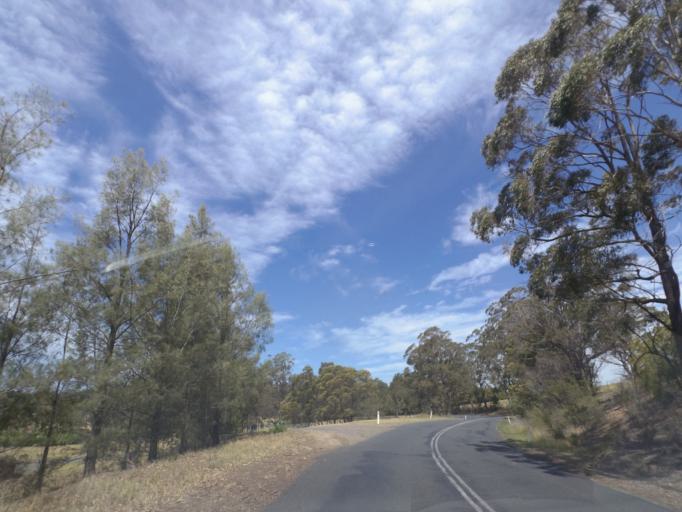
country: AU
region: New South Wales
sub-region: Wingecarribee
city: Colo Vale
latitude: -34.4084
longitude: 150.5173
